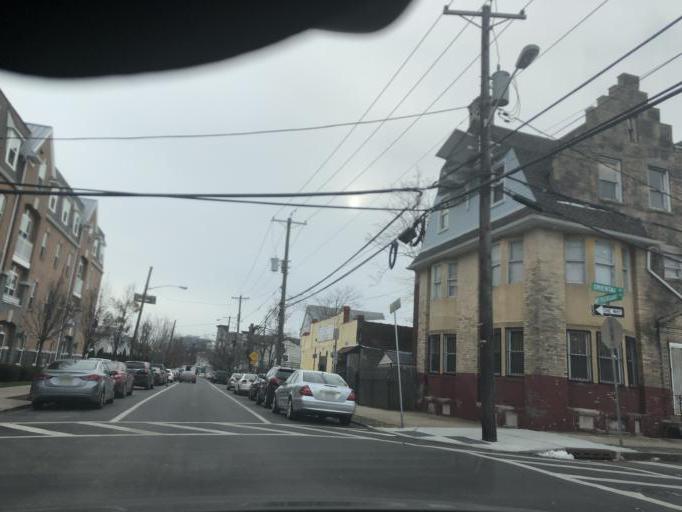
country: US
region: New Jersey
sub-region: Hudson County
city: East Newark
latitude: 40.7602
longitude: -74.1665
